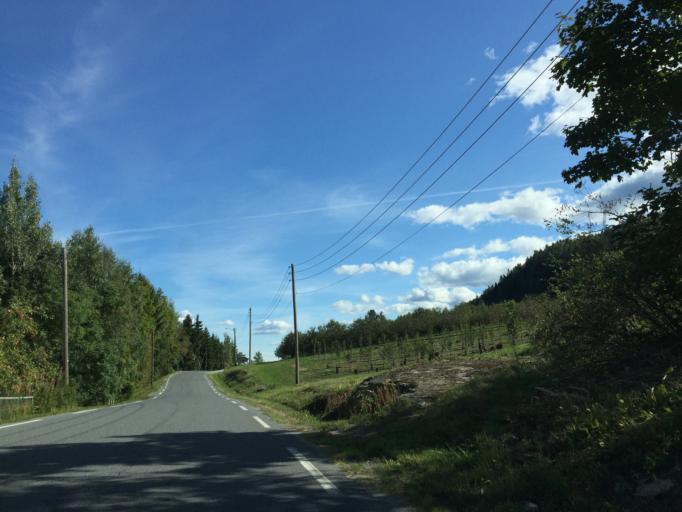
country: NO
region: Buskerud
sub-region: Ovre Eiker
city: Hokksund
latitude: 59.6863
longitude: 9.8536
